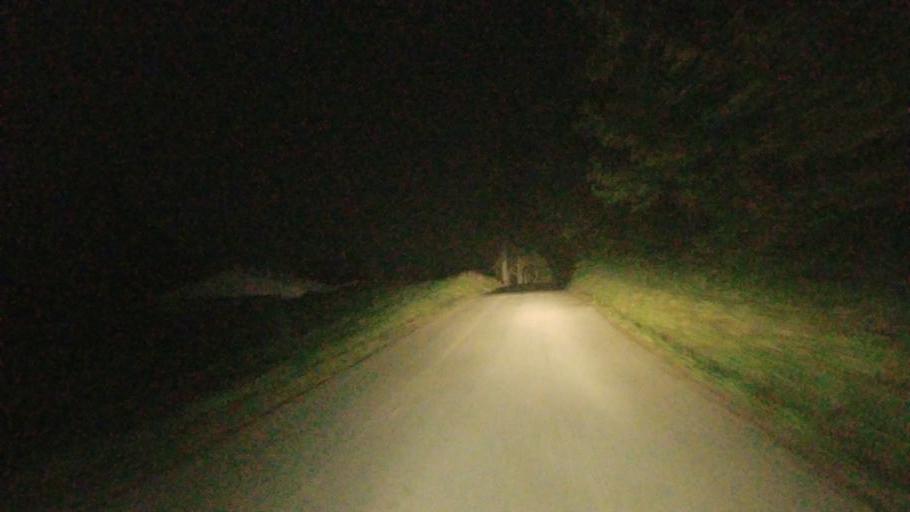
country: US
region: Ohio
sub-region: Harrison County
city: Cadiz
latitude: 40.3925
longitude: -81.1054
